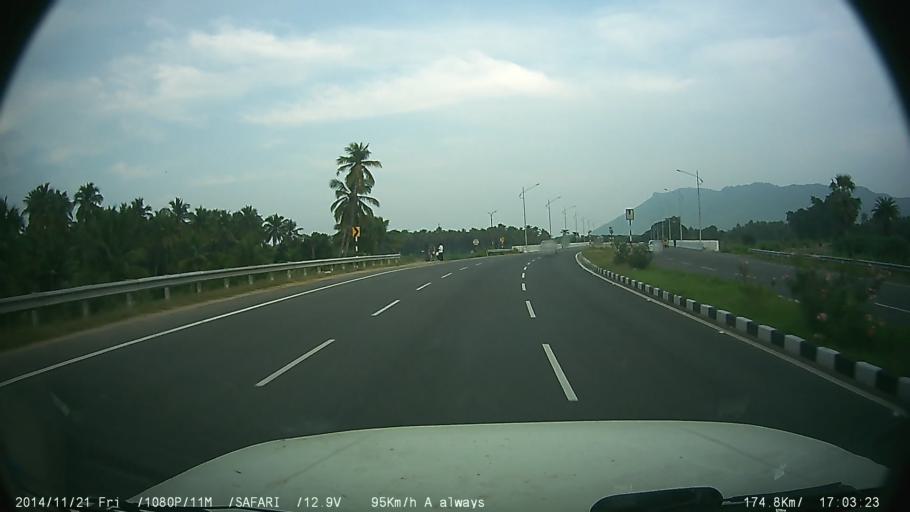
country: IN
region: Tamil Nadu
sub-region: Vellore
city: Pallikondai
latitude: 12.8951
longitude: 78.9138
